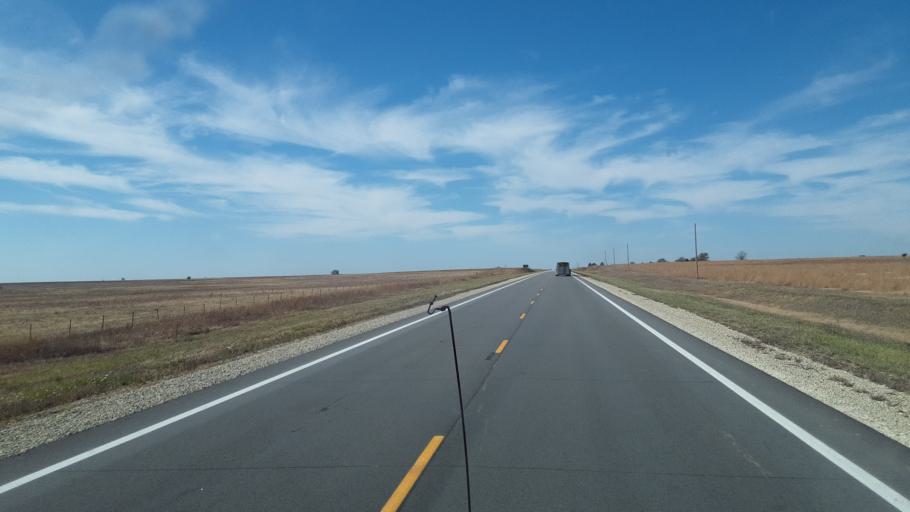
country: US
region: Kansas
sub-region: Marion County
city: Marion
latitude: 38.3629
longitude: -96.8205
